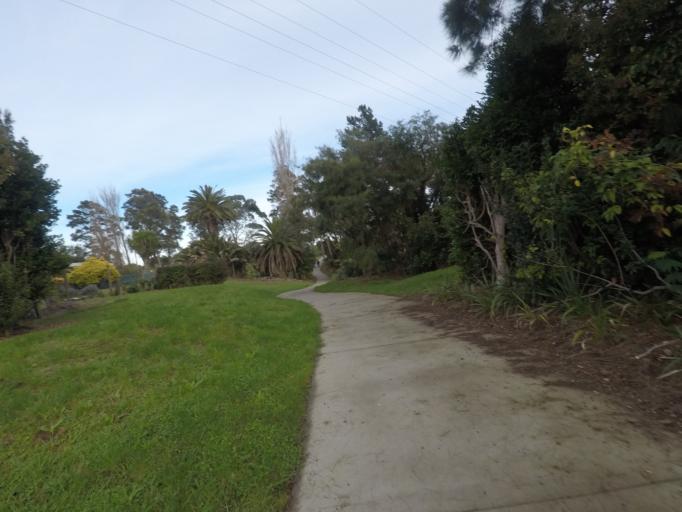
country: NZ
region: Auckland
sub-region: Auckland
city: Mangere
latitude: -36.9483
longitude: 174.8028
